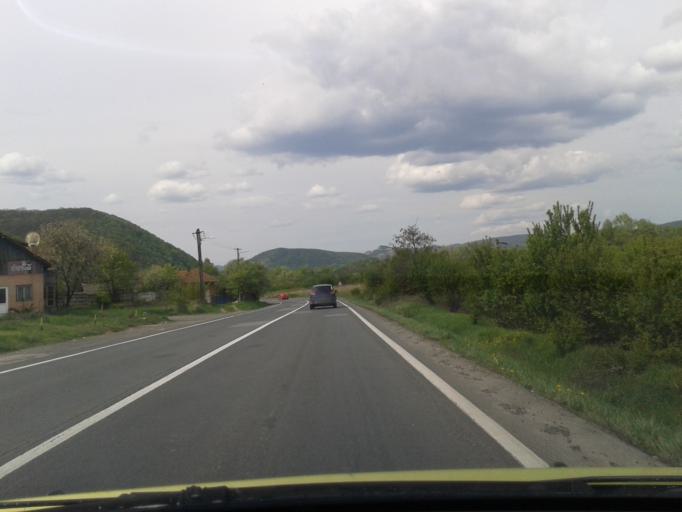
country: RO
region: Hunedoara
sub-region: Comuna Branisca
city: Branisca
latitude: 45.9038
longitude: 22.7877
